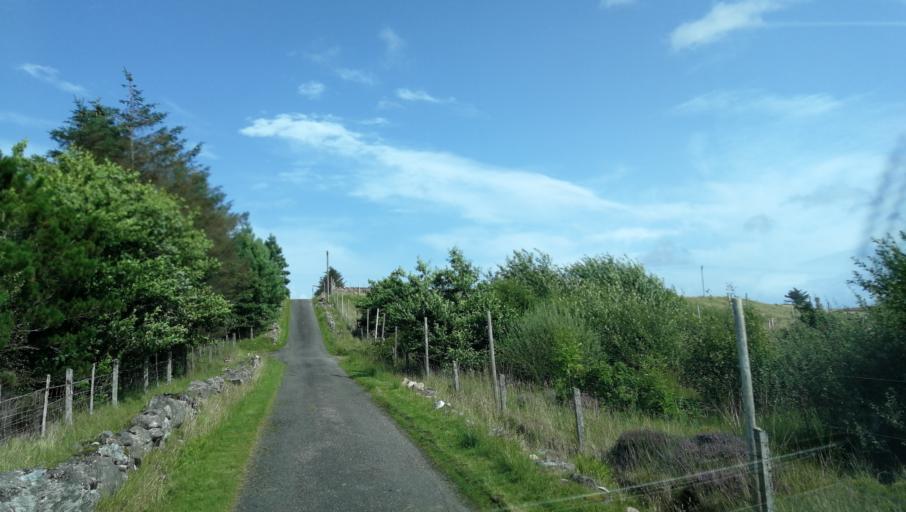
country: GB
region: Scotland
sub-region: Highland
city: Portree
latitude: 57.7441
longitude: -5.7761
